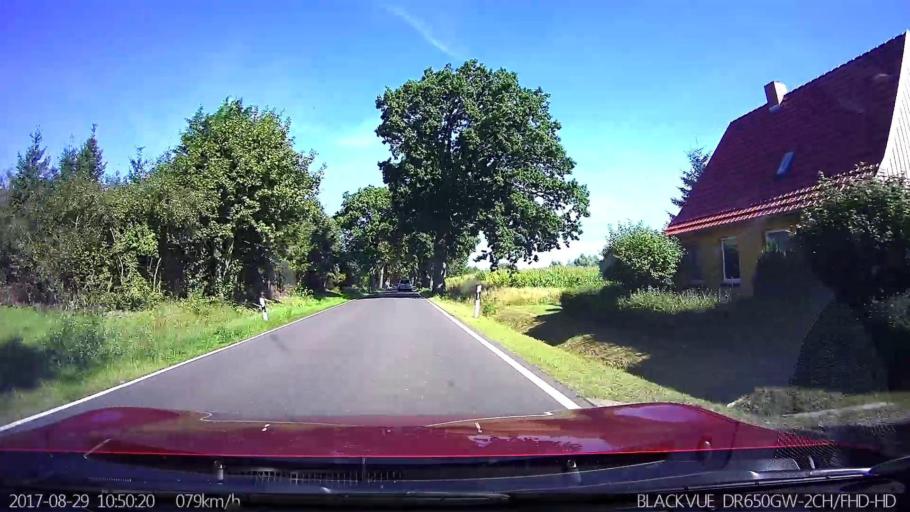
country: DE
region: Mecklenburg-Vorpommern
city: Velgast
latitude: 54.2585
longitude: 12.8212
